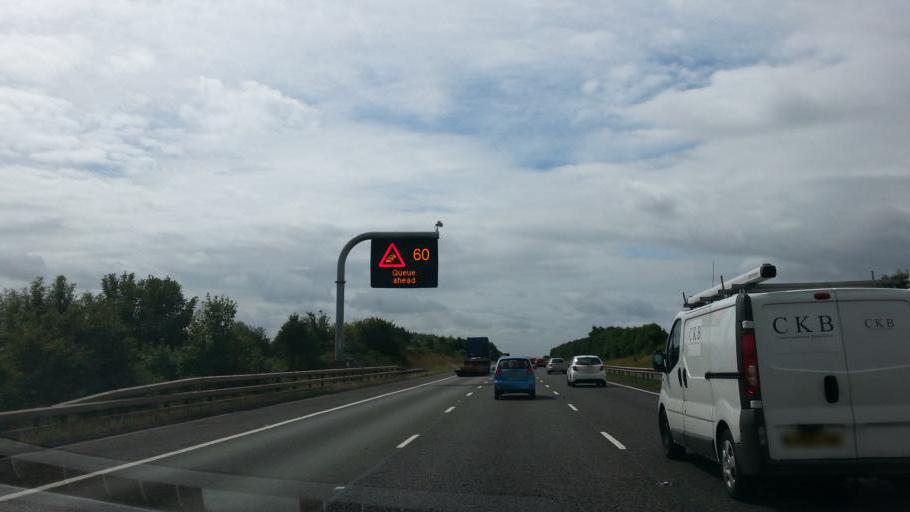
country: GB
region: England
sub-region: Oxfordshire
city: Bicester
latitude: 51.9030
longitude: -1.2059
